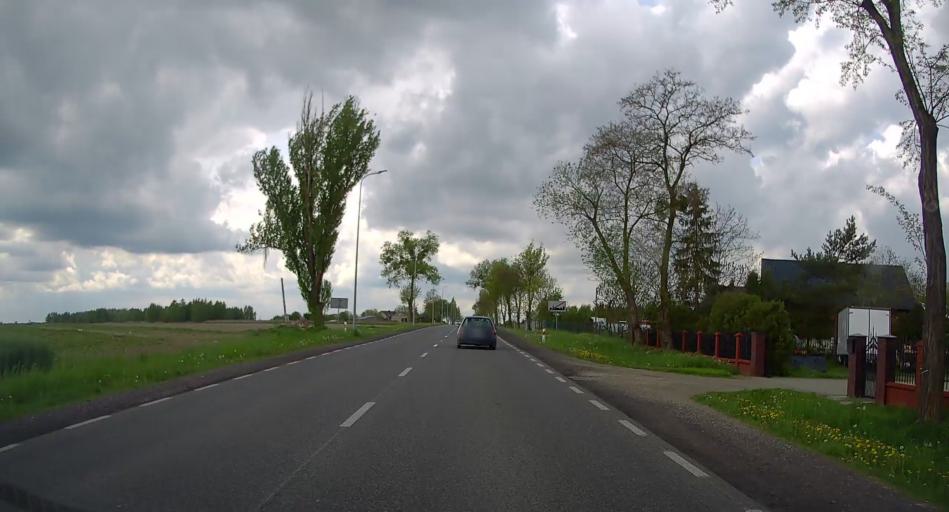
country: PL
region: Masovian Voivodeship
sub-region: Powiat plonski
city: Zaluski
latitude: 52.4451
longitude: 20.4958
